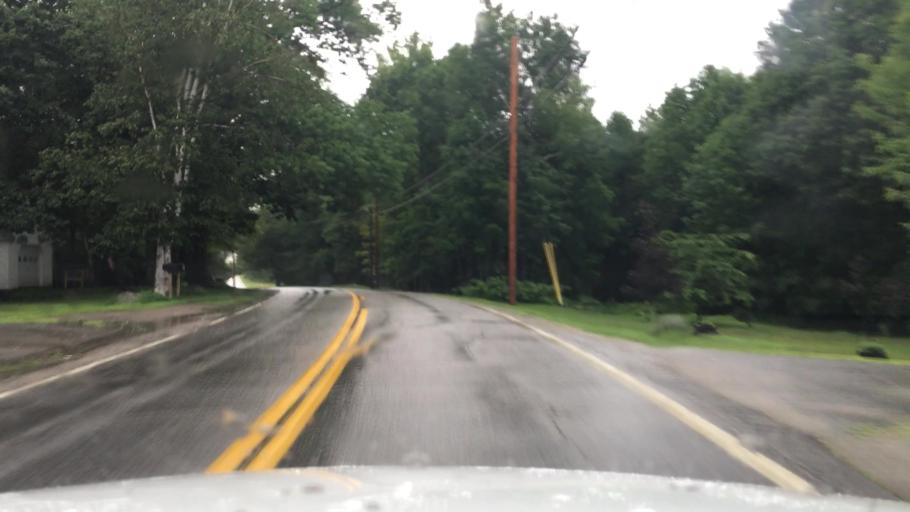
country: US
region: Maine
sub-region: Kennebec County
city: Winthrop
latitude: 44.2846
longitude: -69.9287
